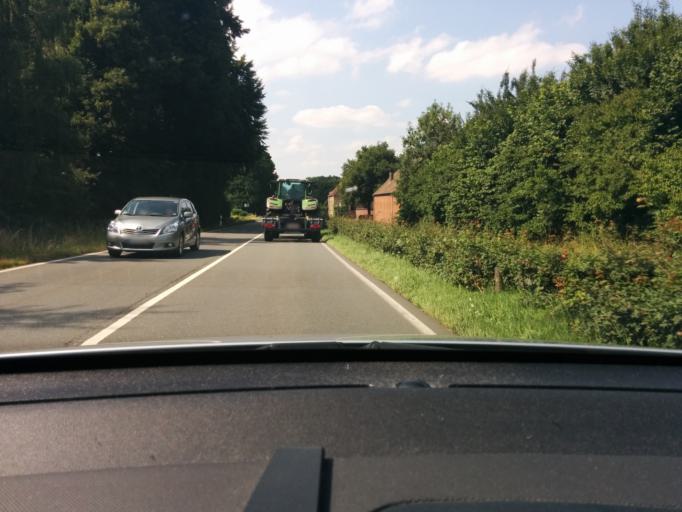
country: DE
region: North Rhine-Westphalia
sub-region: Regierungsbezirk Munster
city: Wettringen
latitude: 52.1713
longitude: 7.2890
